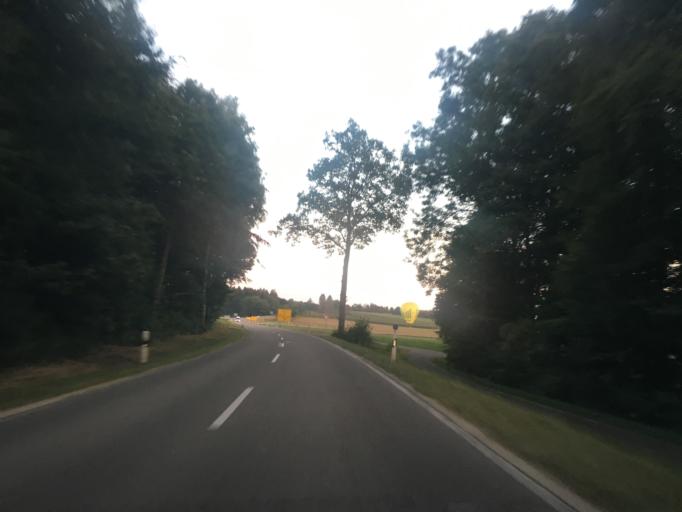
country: DE
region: Baden-Wuerttemberg
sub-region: Tuebingen Region
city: Hayingen
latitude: 48.3000
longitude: 9.4521
